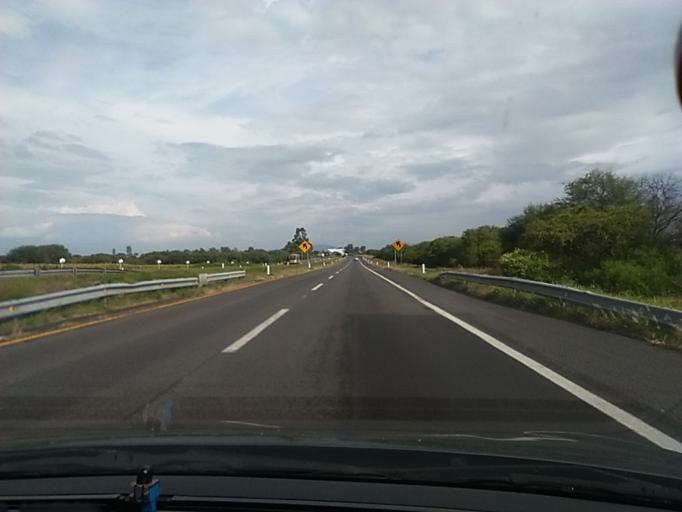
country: MX
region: Jalisco
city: La Barca
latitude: 20.3267
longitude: -102.5809
